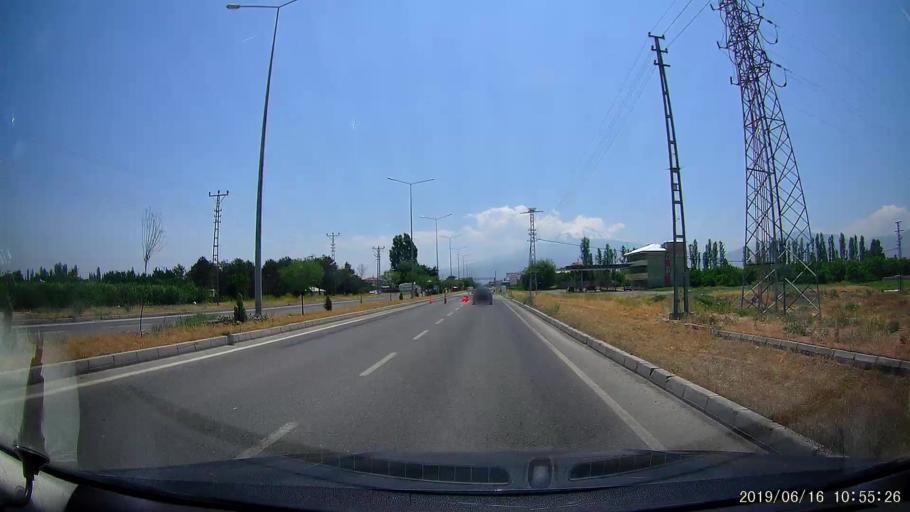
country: TR
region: Igdir
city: Igdir
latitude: 39.9361
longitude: 44.0106
